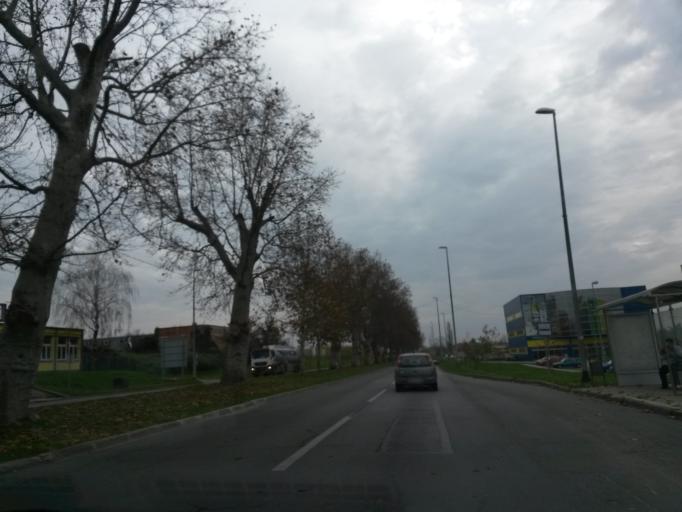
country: HR
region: Vukovarsko-Srijemska
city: Borovo
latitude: 45.3679
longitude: 18.9677
